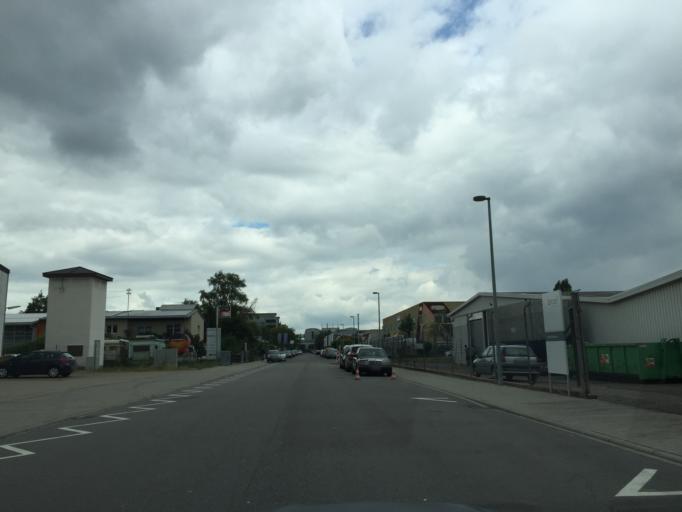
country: DE
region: Baden-Wuerttemberg
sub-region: Karlsruhe Region
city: Walldorf
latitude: 49.2903
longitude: 8.6488
